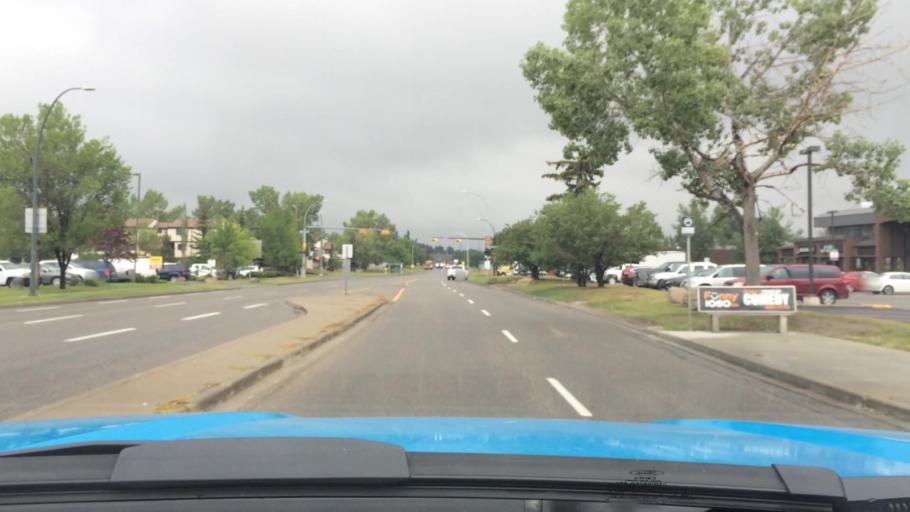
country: CA
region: Alberta
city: Calgary
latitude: 51.0964
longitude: -114.0539
